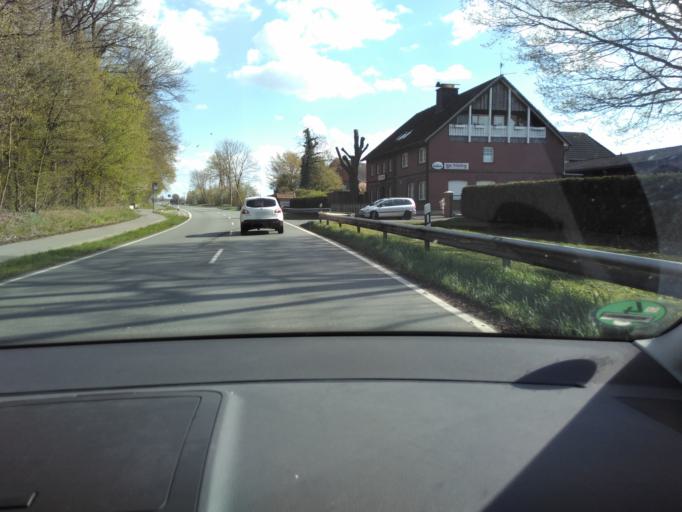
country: DE
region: North Rhine-Westphalia
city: Oelde
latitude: 51.7984
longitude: 8.1356
